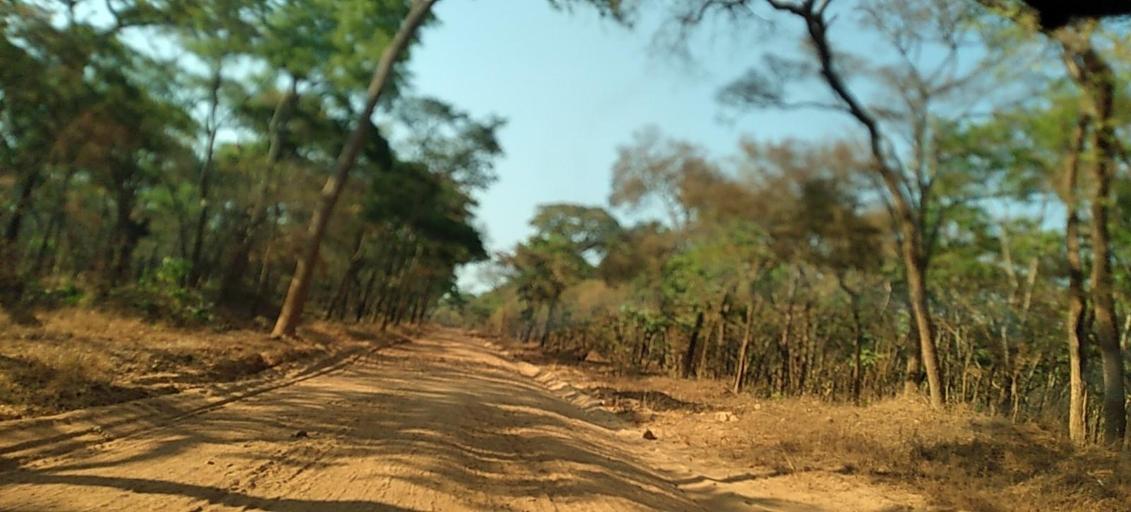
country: ZM
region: North-Western
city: Kasempa
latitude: -13.6137
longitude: 25.9790
